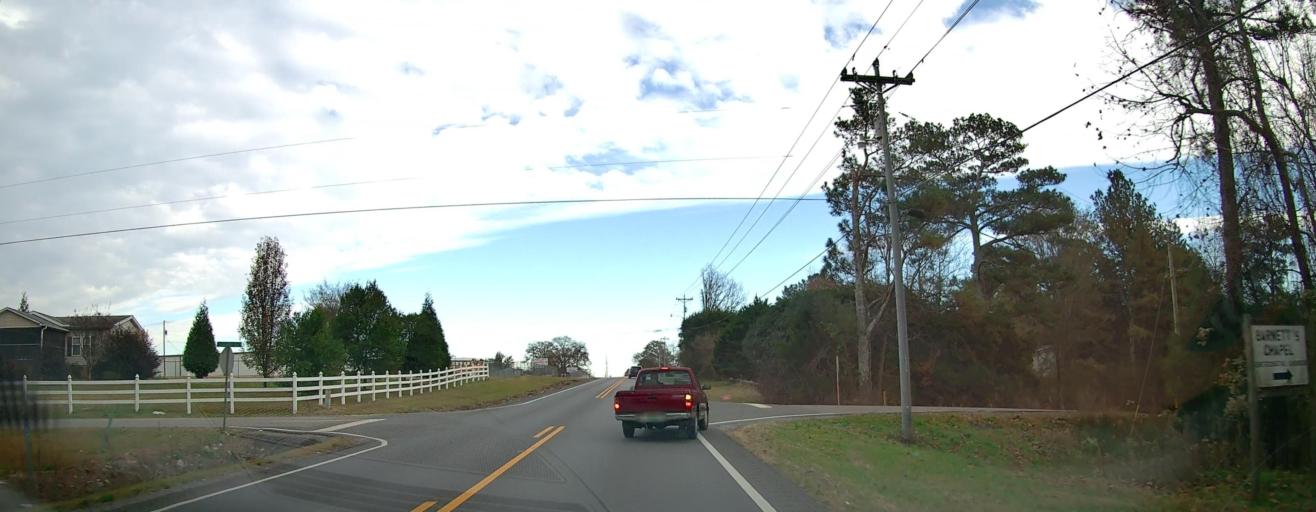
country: US
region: Alabama
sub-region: Morgan County
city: Priceville
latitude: 34.4746
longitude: -86.8085
